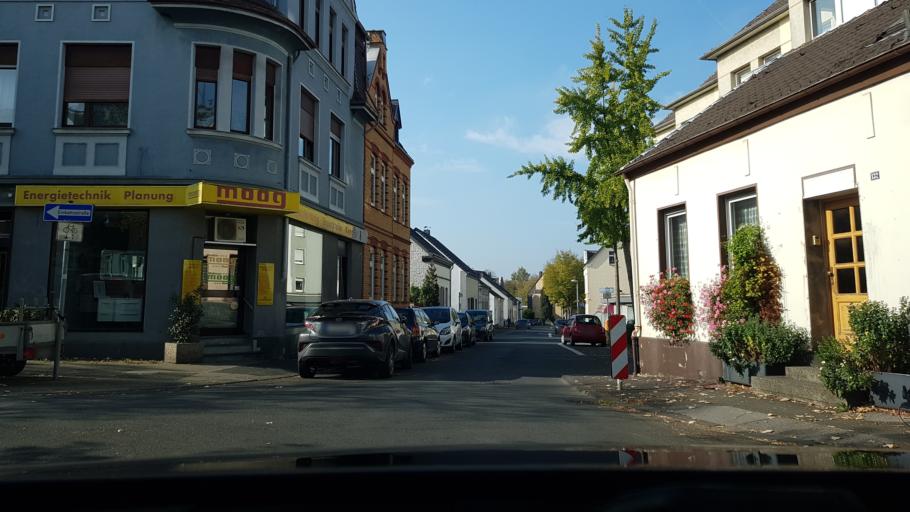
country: DE
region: North Rhine-Westphalia
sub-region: Regierungsbezirk Dusseldorf
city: Muelheim (Ruhr)
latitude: 51.4248
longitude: 6.8592
